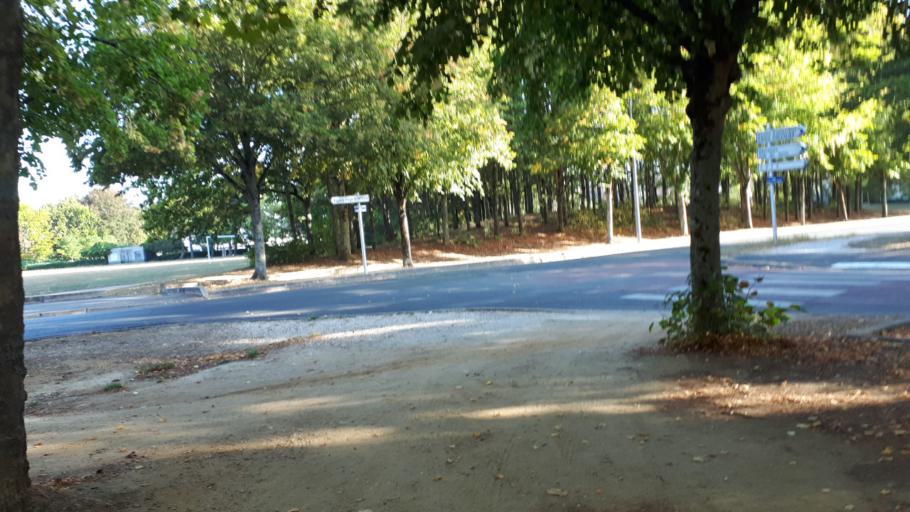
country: FR
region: Centre
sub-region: Departement du Loir-et-Cher
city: Blois
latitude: 47.5935
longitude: 1.3055
